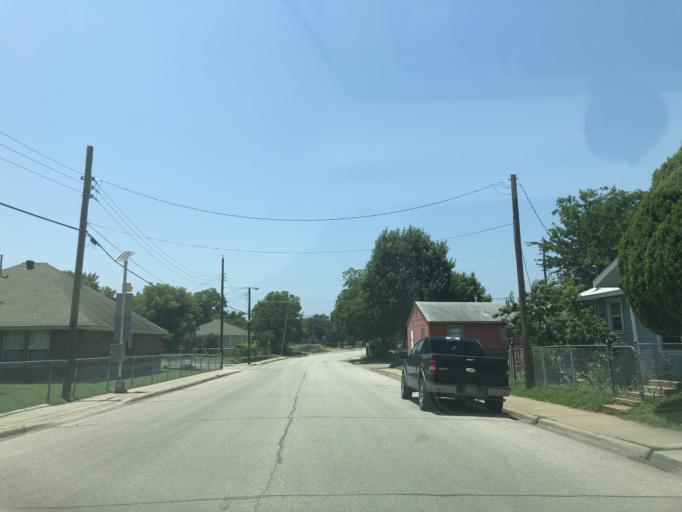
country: US
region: Texas
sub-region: Dallas County
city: Dallas
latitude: 32.7814
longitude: -96.8402
